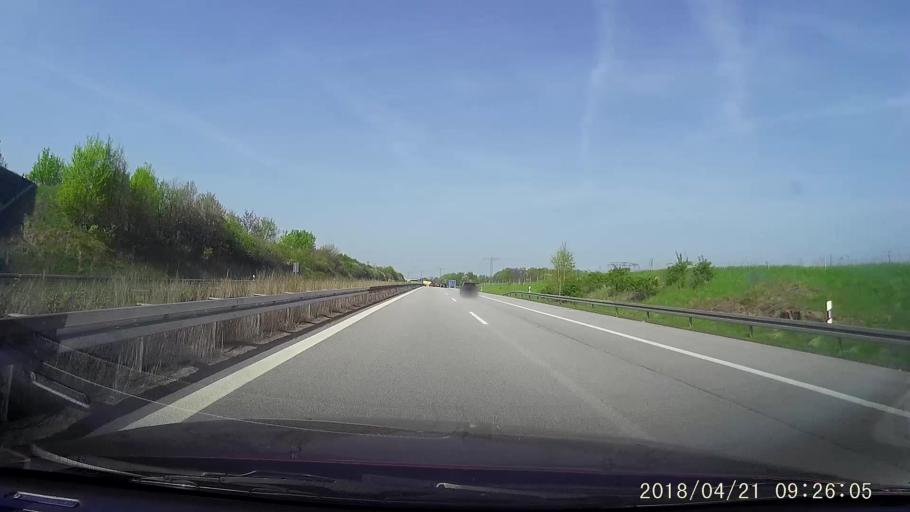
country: DE
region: Saxony
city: Bautzen
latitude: 51.1955
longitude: 14.4565
